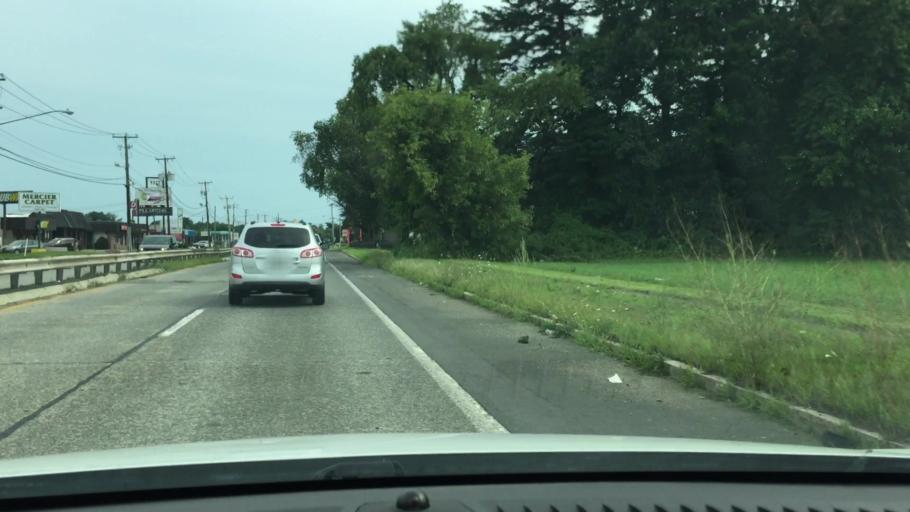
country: US
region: Massachusetts
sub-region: Hampden County
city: Chicopee
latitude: 42.1409
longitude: -72.6273
